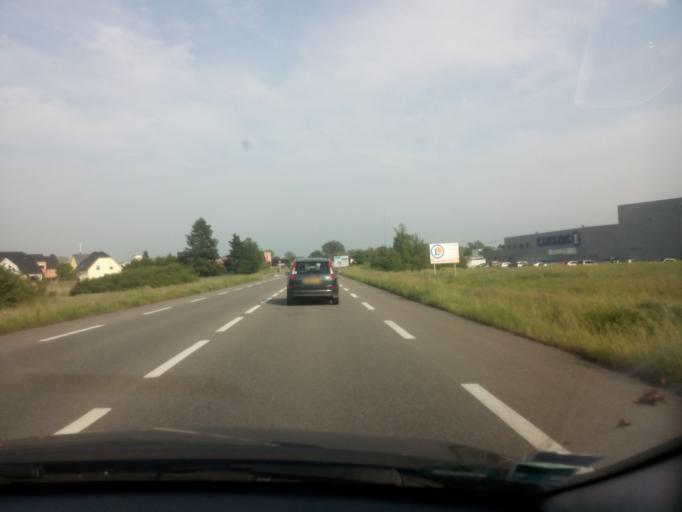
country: FR
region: Alsace
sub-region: Departement du Bas-Rhin
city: Soufflenheim
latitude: 48.8211
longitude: 7.9612
